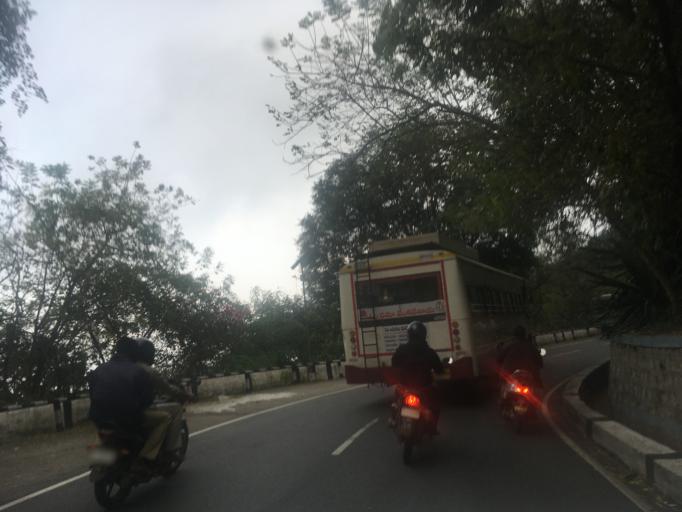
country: IN
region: Andhra Pradesh
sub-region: Chittoor
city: Tirumala
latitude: 13.6673
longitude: 79.3481
